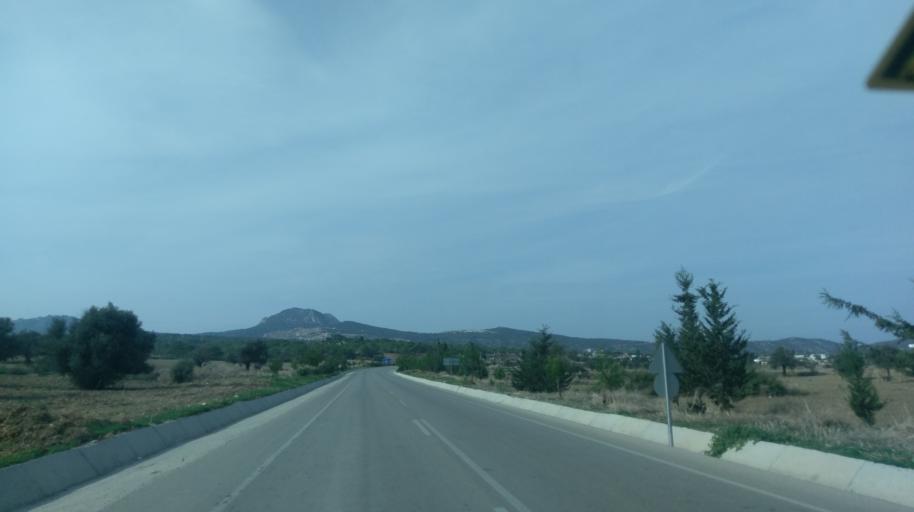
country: CY
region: Ammochostos
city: Trikomo
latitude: 35.4013
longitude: 33.9955
